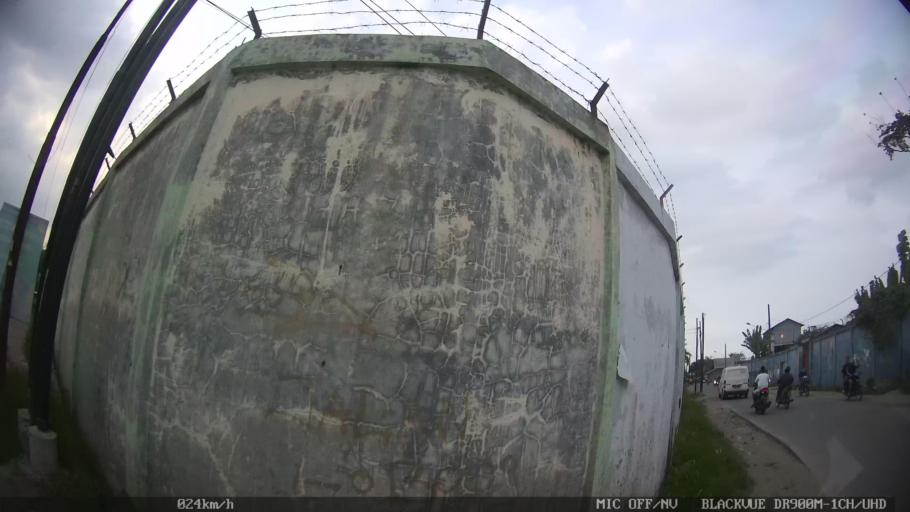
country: ID
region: North Sumatra
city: Sunggal
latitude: 3.5677
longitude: 98.6107
